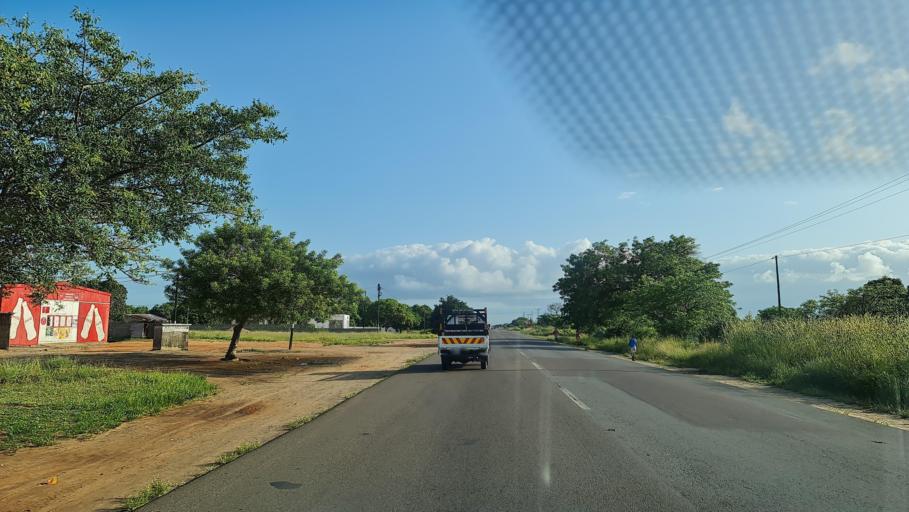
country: MZ
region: Maputo City
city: Maputo
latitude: -25.6867
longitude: 32.6650
